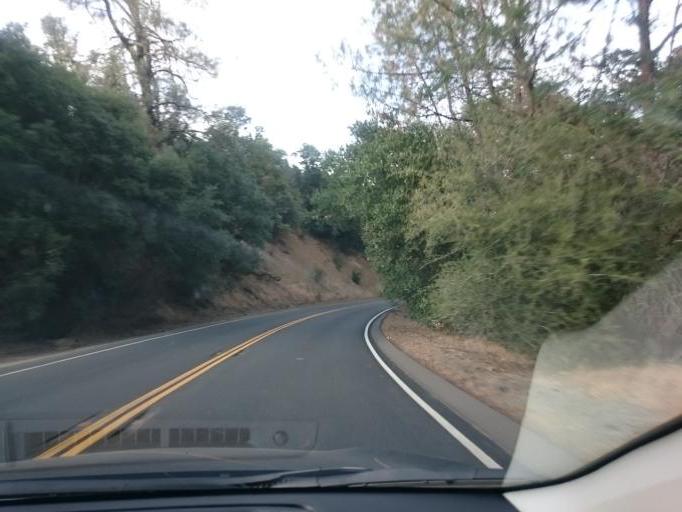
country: US
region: California
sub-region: Yolo County
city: Winters
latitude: 38.4806
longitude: -122.1351
